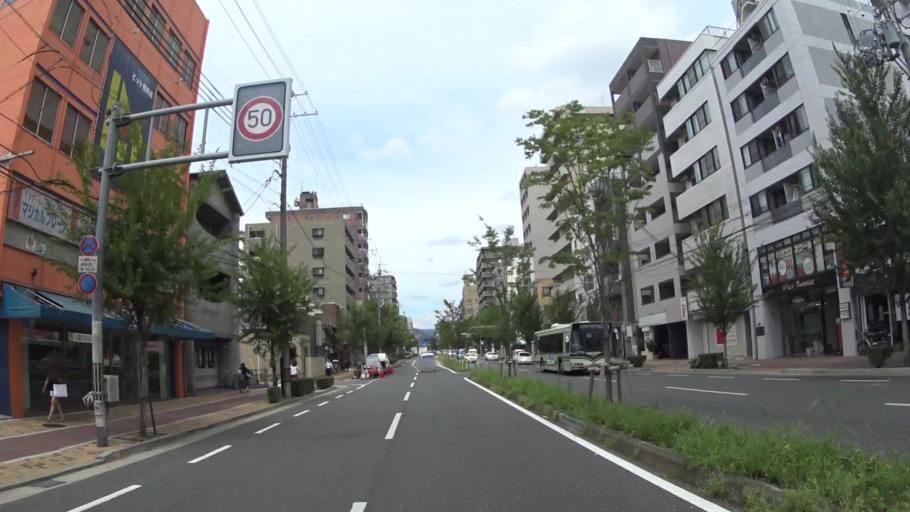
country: JP
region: Kyoto
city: Kyoto
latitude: 35.0047
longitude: 135.7319
